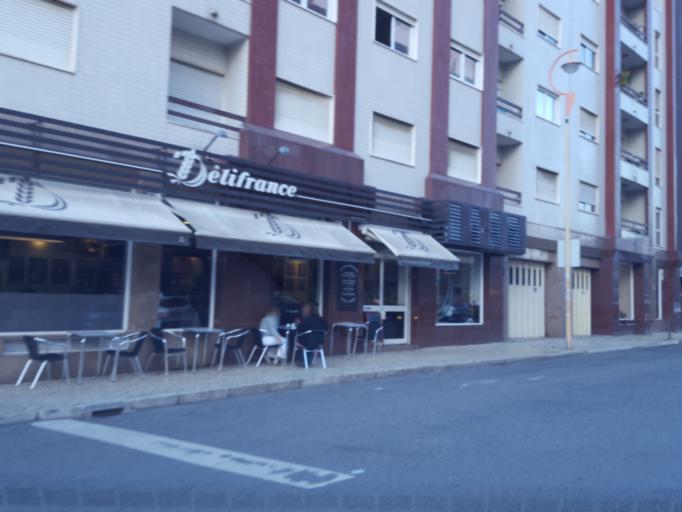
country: PT
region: Lisbon
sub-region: Odivelas
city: Pontinha
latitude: 38.7506
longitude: -9.1731
